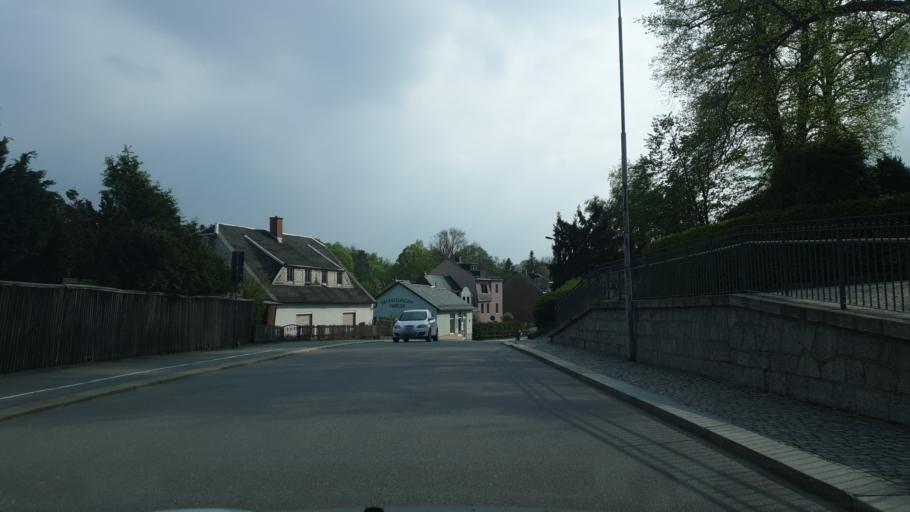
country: DE
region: Saxony
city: Stollberg
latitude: 50.7045
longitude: 12.7757
